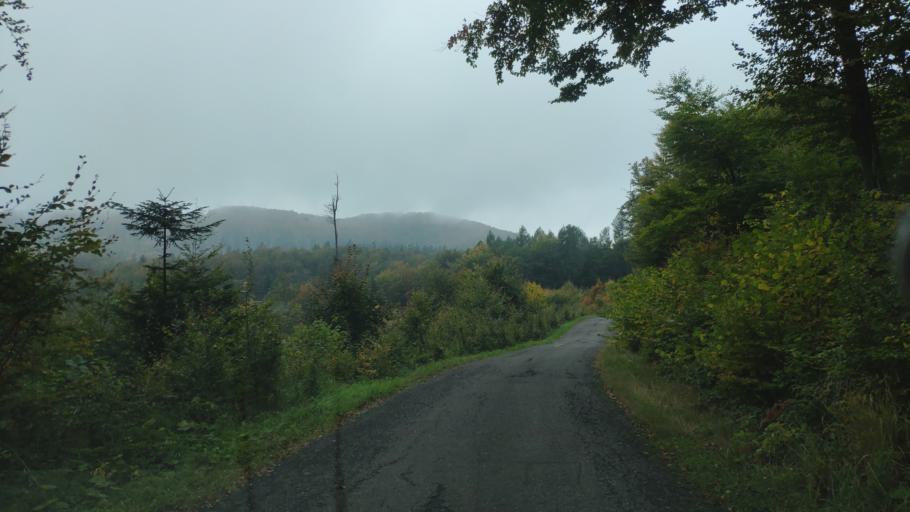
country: SK
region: Presovsky
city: Giraltovce
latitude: 48.9186
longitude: 21.4566
